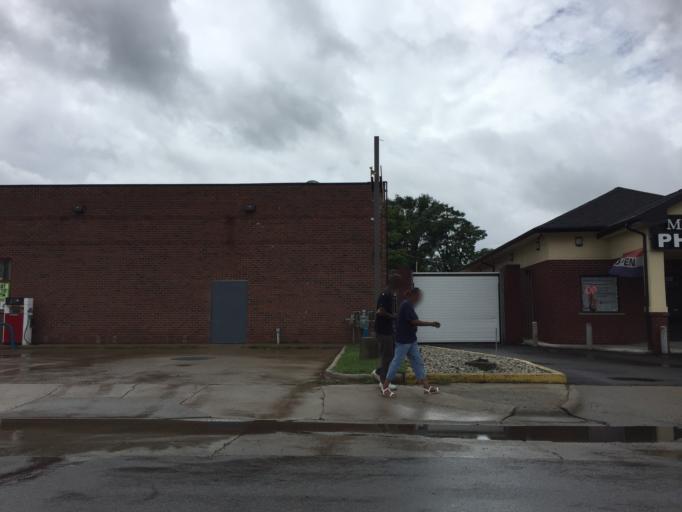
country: US
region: Michigan
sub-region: Oakland County
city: Oak Park
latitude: 42.4025
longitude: -83.1602
